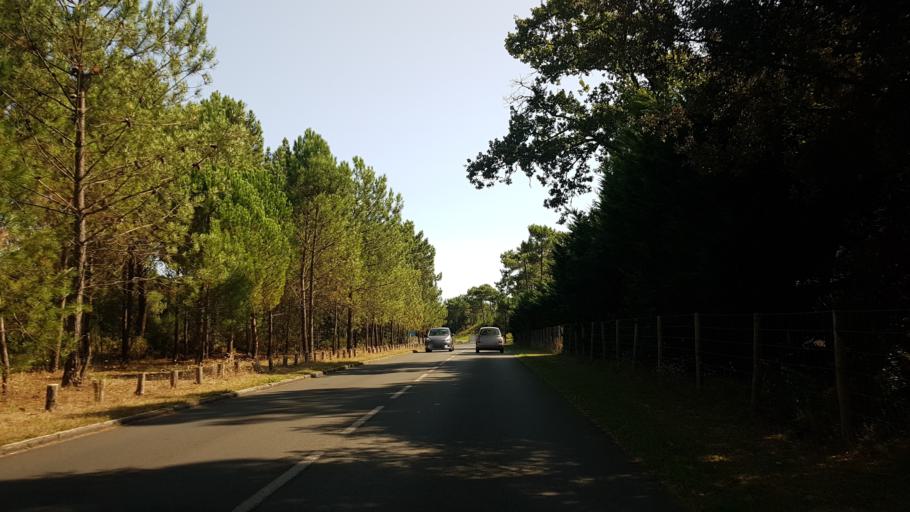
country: FR
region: Poitou-Charentes
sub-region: Departement de la Charente-Maritime
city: Les Mathes
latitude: 45.6974
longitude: -1.1962
